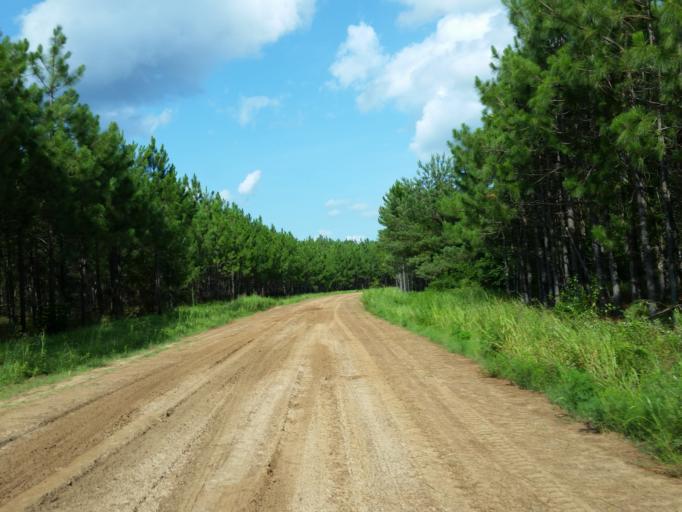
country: US
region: Georgia
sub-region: Lee County
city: Leesburg
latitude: 31.7664
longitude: -84.0379
